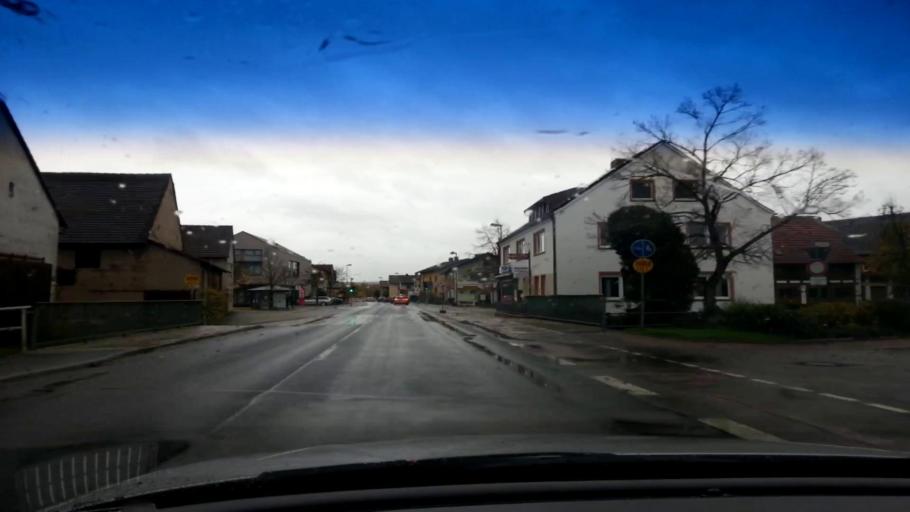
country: DE
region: Bavaria
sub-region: Upper Franconia
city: Viereth-Trunstadt
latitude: 49.9236
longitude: 10.7784
